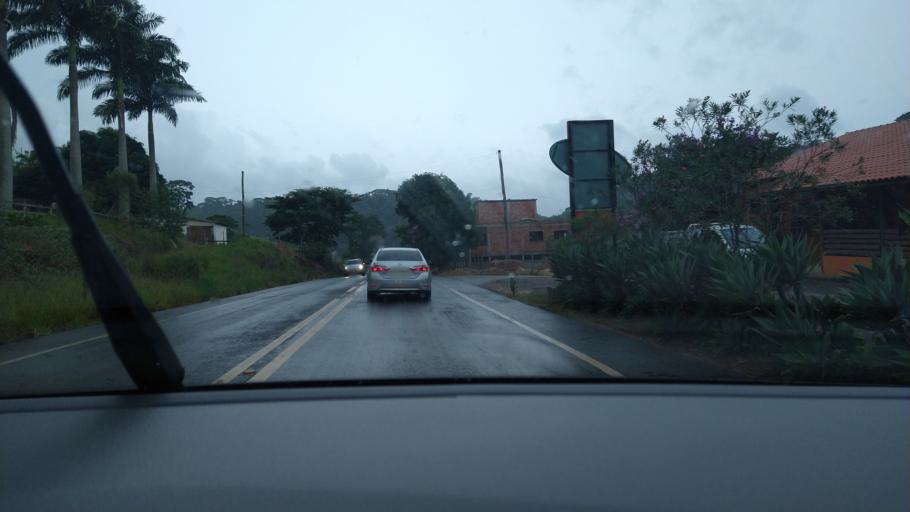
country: BR
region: Minas Gerais
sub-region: Vicosa
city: Vicosa
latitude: -20.6453
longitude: -42.8655
